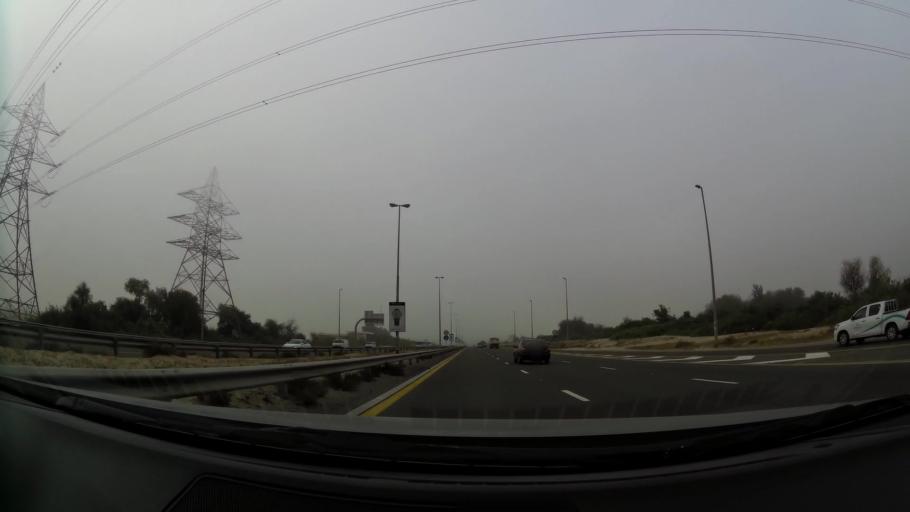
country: AE
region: Dubai
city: Dubai
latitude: 25.1483
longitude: 55.3414
